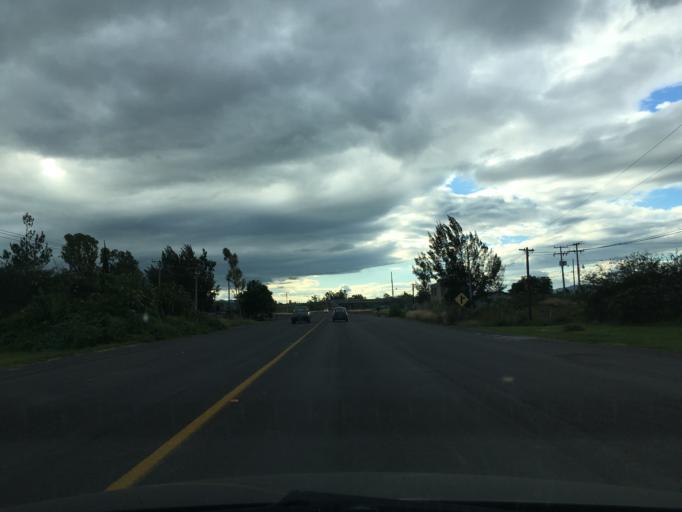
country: MX
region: Michoacan
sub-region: Cuitzeo
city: Cuamio
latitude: 20.0760
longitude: -101.1326
